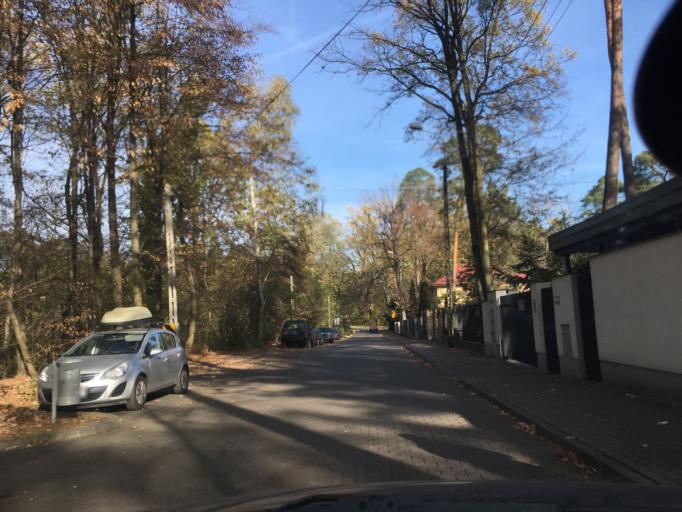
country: PL
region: Masovian Voivodeship
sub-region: Powiat piaseczynski
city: Piaseczno
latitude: 52.0591
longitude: 21.0104
